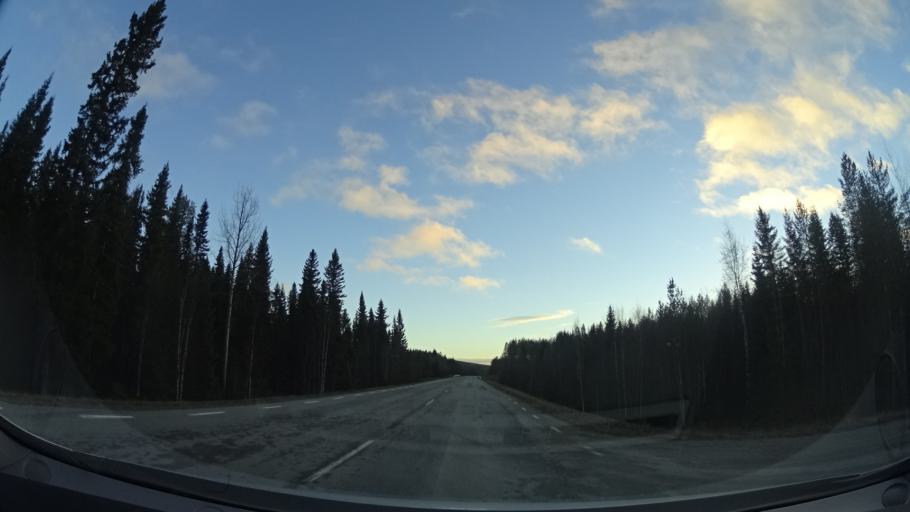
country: SE
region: Jaemtland
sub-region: Stroemsunds Kommun
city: Stroemsund
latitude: 64.0430
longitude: 15.5405
